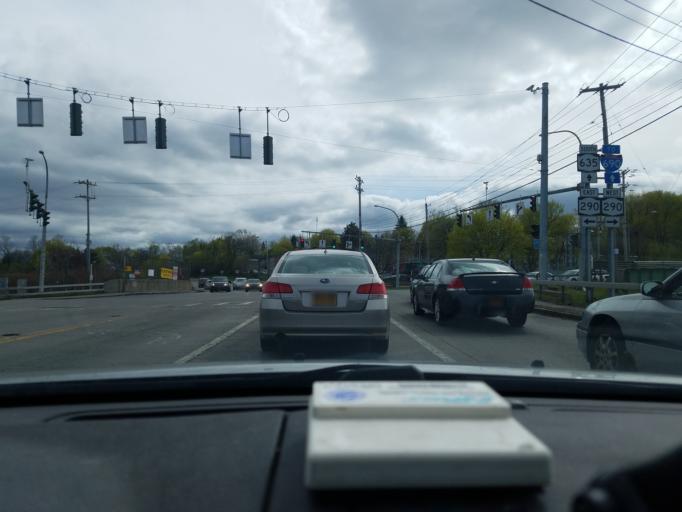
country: US
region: New York
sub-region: Onondaga County
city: East Syracuse
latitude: 43.0699
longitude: -76.0905
